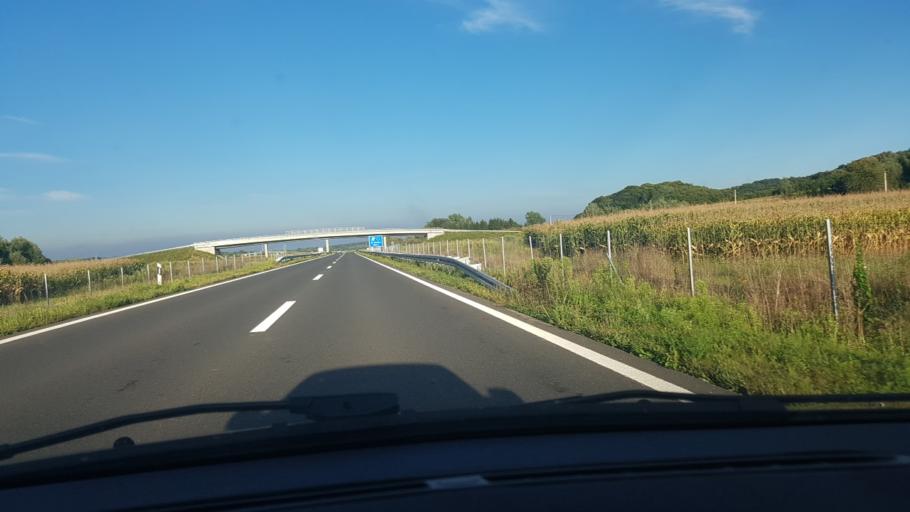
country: HR
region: Krapinsko-Zagorska
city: Selnica
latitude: 46.0391
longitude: 16.0465
